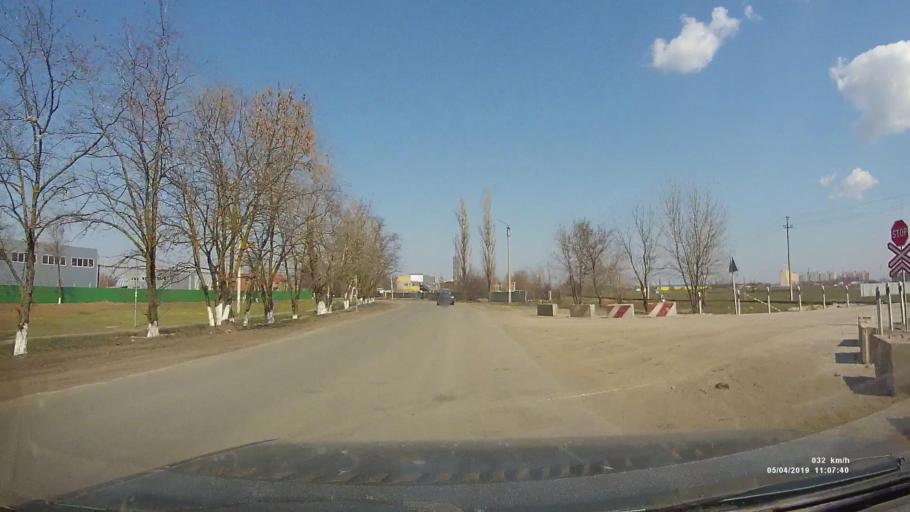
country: RU
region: Rostov
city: Azov
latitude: 47.0819
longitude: 39.4373
